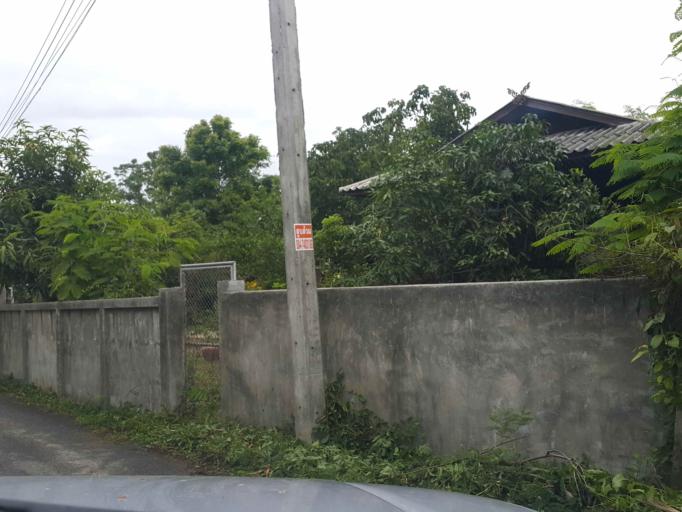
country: TH
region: Chiang Mai
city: San Kamphaeng
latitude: 18.7868
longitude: 99.1057
